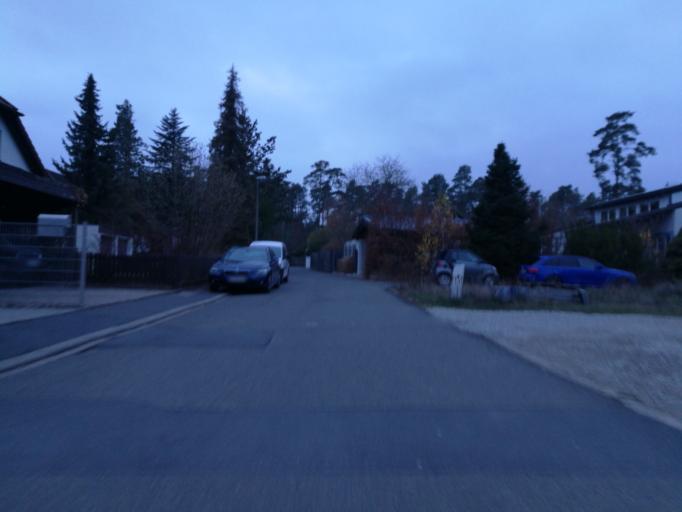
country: DE
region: Bavaria
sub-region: Regierungsbezirk Mittelfranken
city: Seukendorf
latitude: 49.4704
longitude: 10.8845
